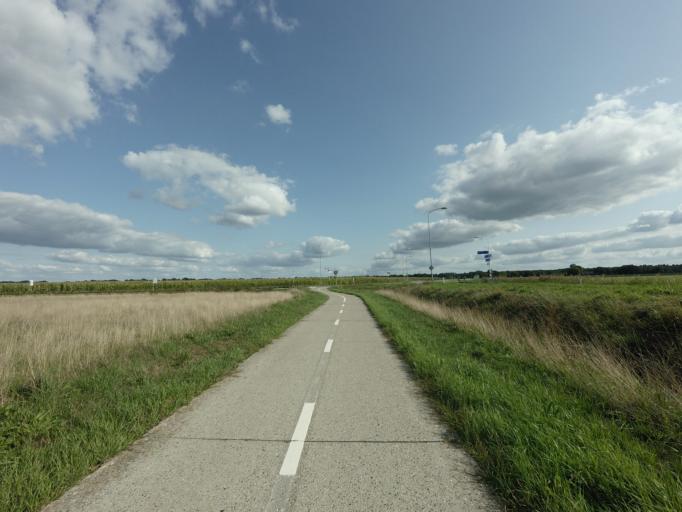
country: NL
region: Drenthe
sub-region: Gemeente Westerveld
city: Dwingeloo
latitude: 52.8389
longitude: 6.3981
